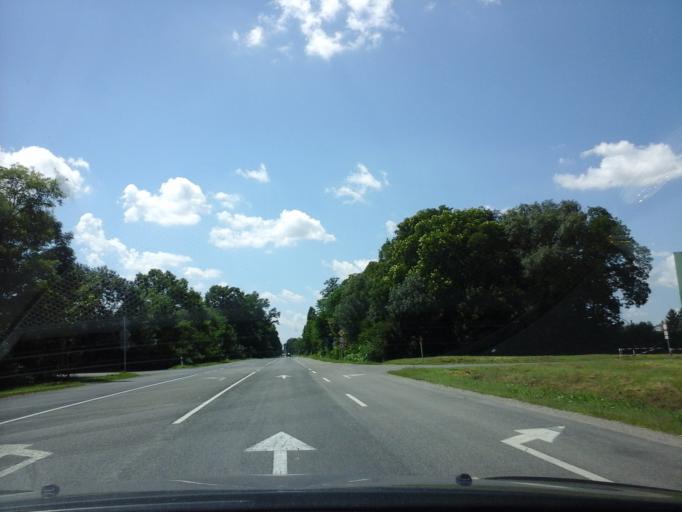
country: HU
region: Hajdu-Bihar
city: Hajduszoboszlo
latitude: 47.4568
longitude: 21.4267
